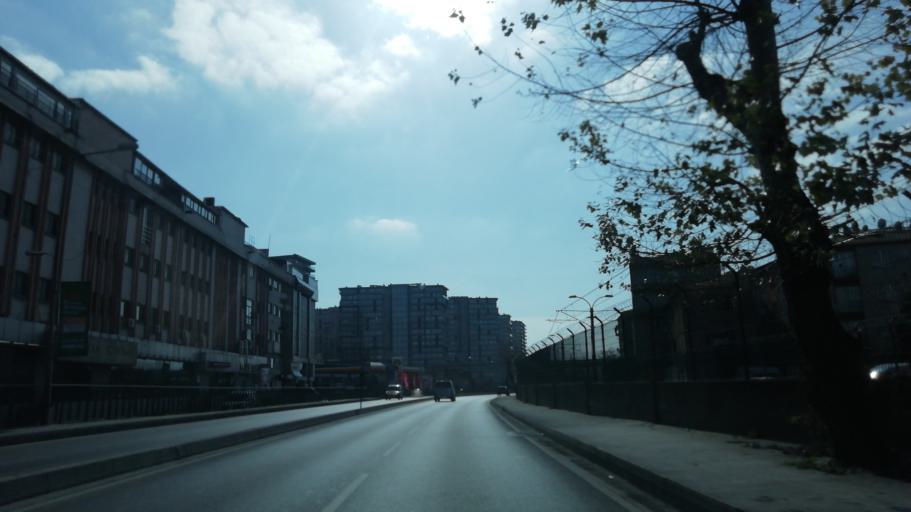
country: TR
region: Istanbul
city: merter keresteciler
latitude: 41.0293
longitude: 28.8987
